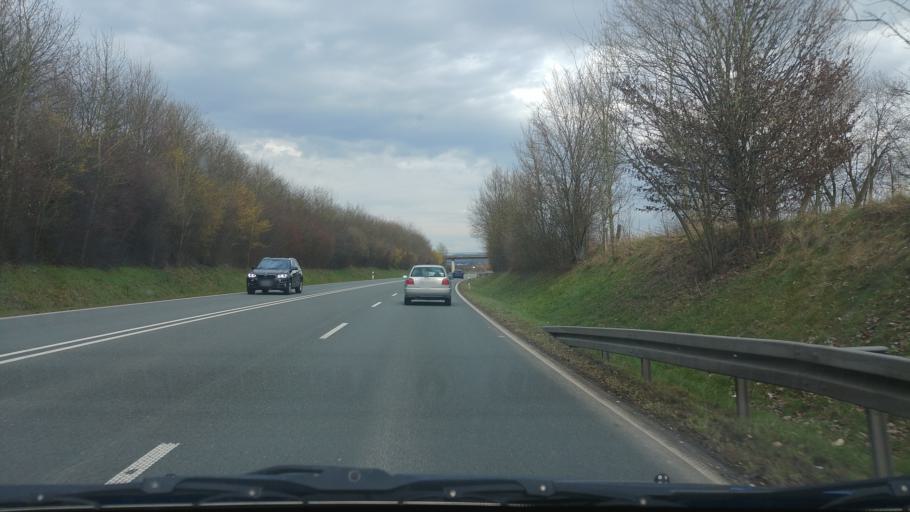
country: DE
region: Lower Saxony
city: Holzminden
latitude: 51.8176
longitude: 9.4063
